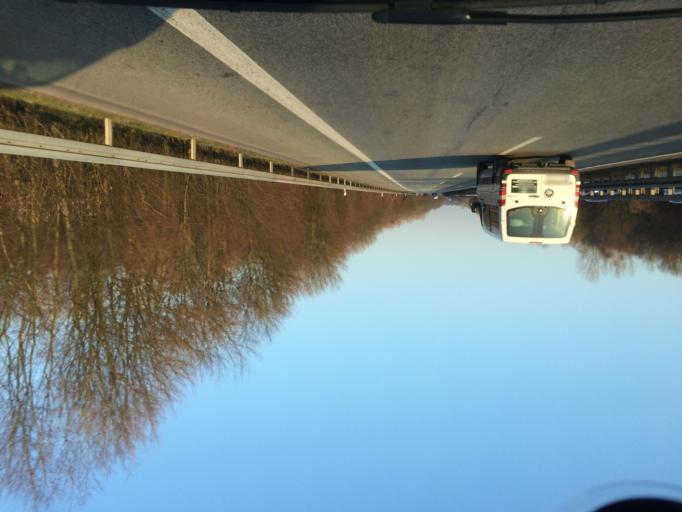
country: DE
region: North Rhine-Westphalia
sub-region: Regierungsbezirk Munster
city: Dulmen
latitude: 51.8282
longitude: 7.2341
